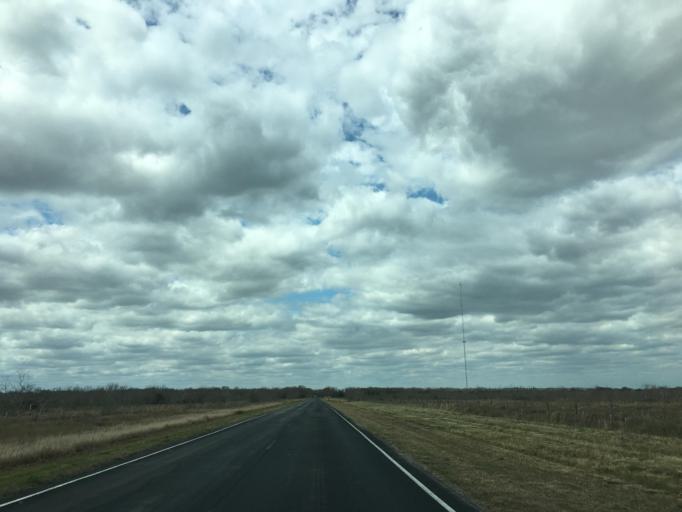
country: US
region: Texas
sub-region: Brazoria County
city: Oyster Creek
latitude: 29.0653
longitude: -95.3109
